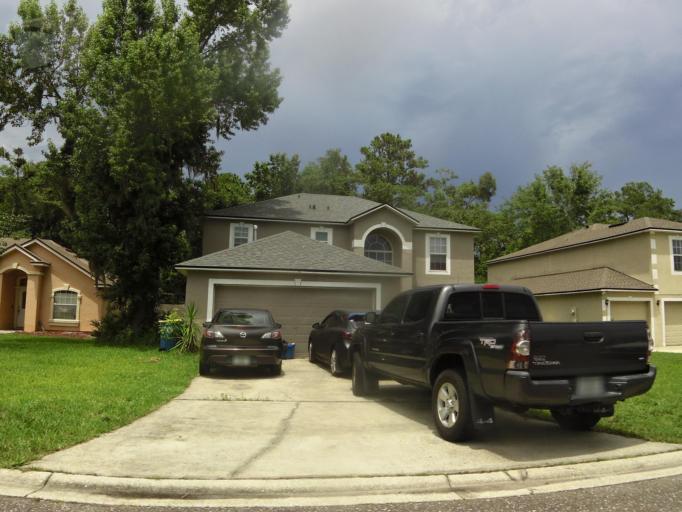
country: US
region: Florida
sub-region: Duval County
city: Jacksonville
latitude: 30.4259
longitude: -81.7258
